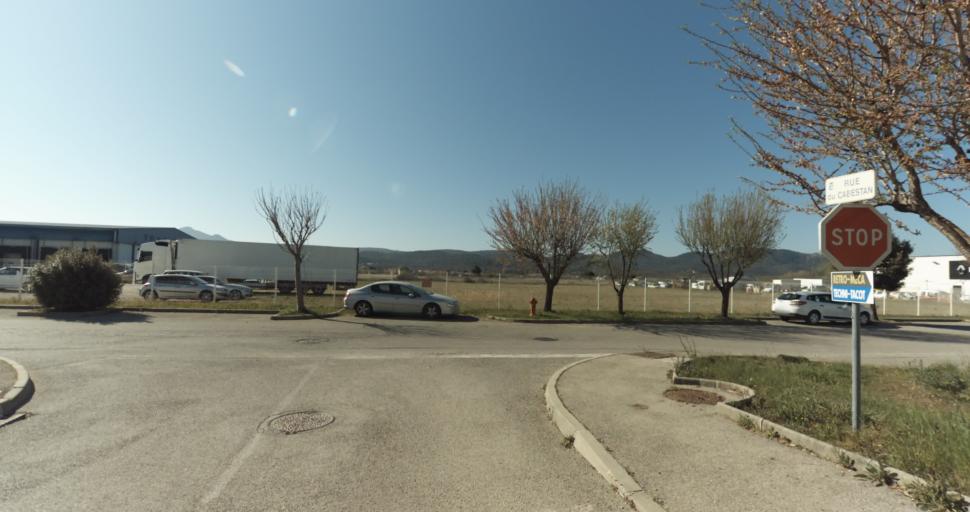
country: FR
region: Provence-Alpes-Cote d'Azur
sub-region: Departement des Bouches-du-Rhone
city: Peyrolles-en-Provence
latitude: 43.6563
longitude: 5.5780
